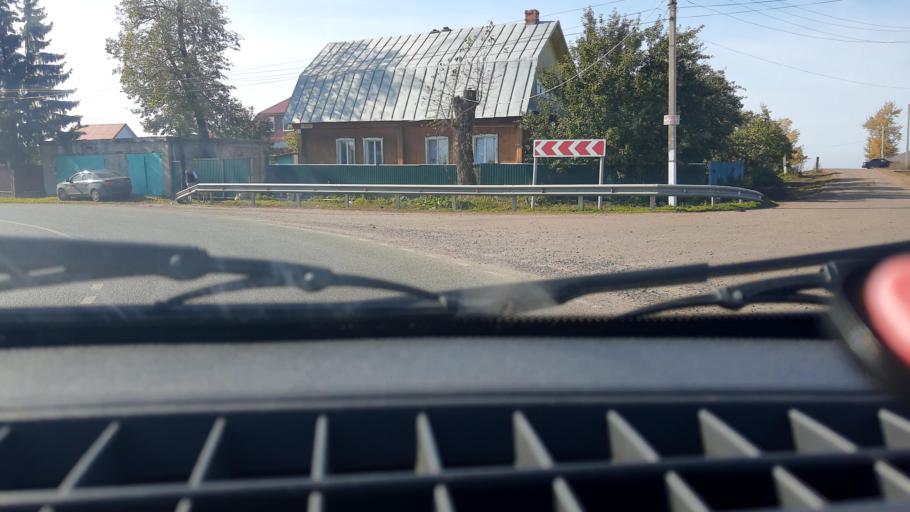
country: RU
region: Bashkortostan
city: Avdon
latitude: 54.5609
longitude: 55.6549
